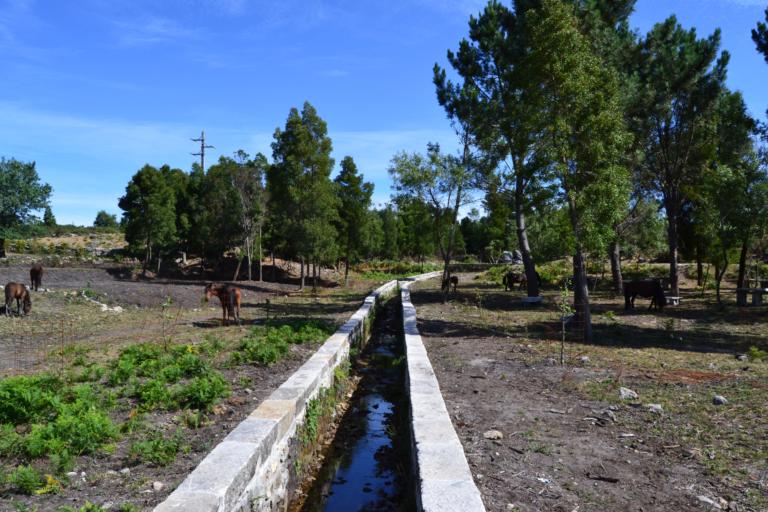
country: PT
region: Viana do Castelo
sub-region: Viana do Castelo
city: Meadela
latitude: 41.7537
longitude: -8.8163
